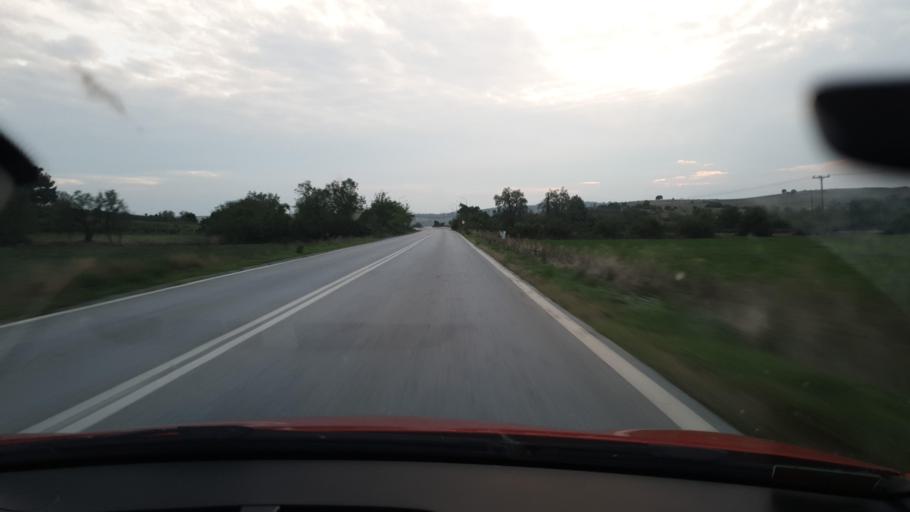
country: GR
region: Central Macedonia
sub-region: Nomos Kilkis
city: Kristoni
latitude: 40.9978
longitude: 22.7640
